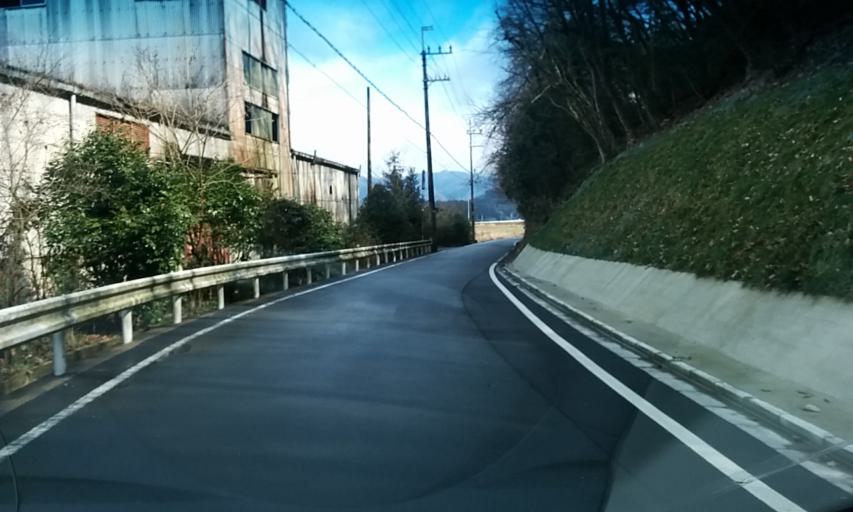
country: JP
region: Kyoto
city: Ayabe
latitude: 35.1800
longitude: 135.4136
